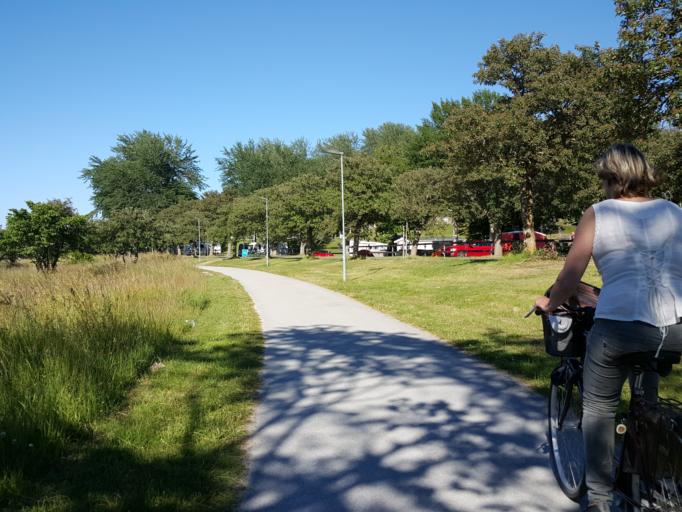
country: SE
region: Gotland
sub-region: Gotland
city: Visby
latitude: 57.6546
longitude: 18.3062
